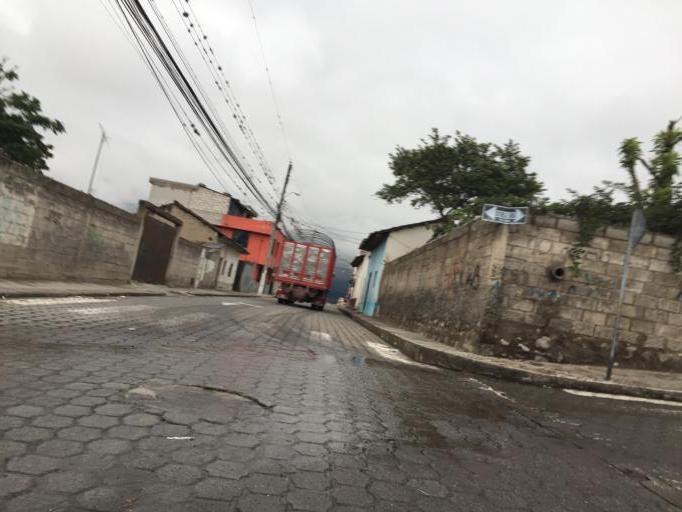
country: EC
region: Imbabura
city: Atuntaqui
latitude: 0.3364
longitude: -78.1717
